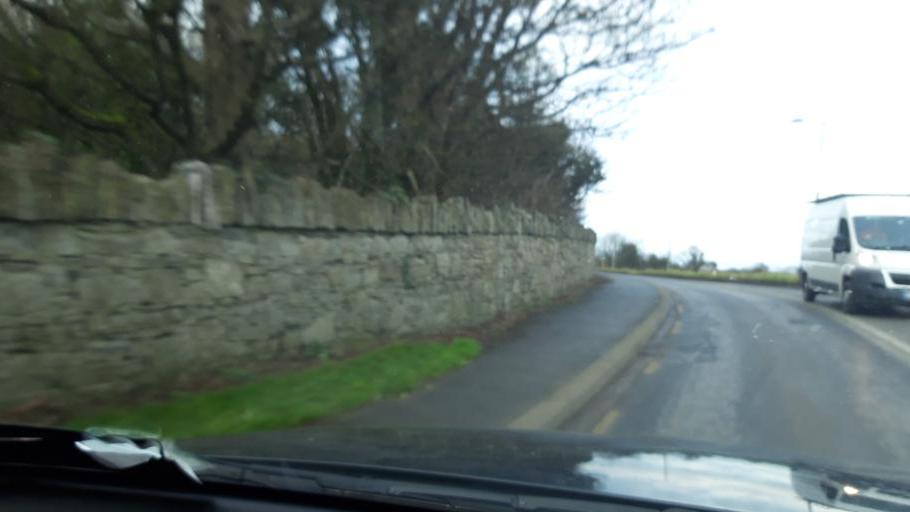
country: IE
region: Leinster
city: An Ros
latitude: 53.5372
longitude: -6.0907
